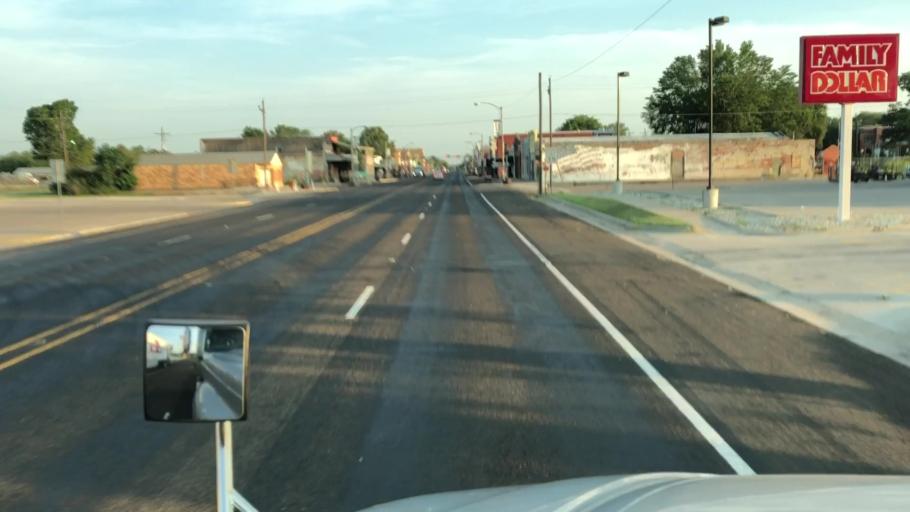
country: US
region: Texas
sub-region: Robertson County
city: Calvert
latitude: 30.9768
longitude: -96.6728
